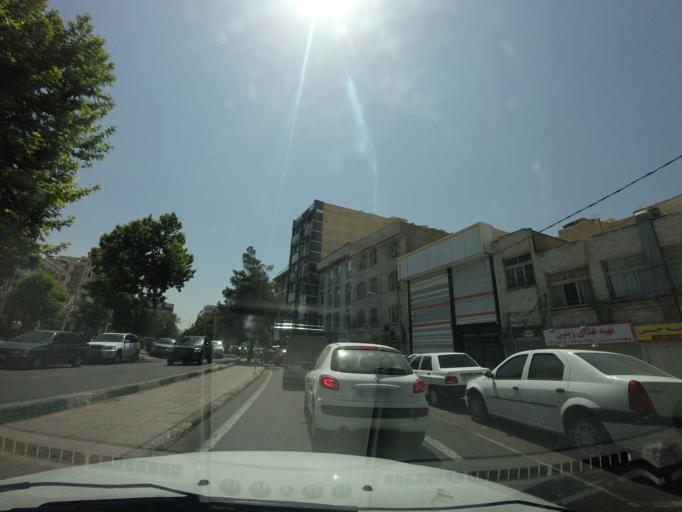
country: IR
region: Tehran
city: Tehran
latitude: 35.7242
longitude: 51.3130
